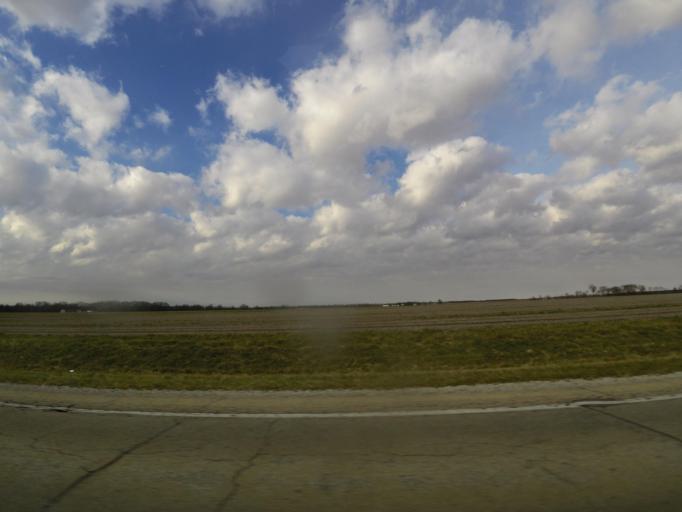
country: US
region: Illinois
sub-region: Fayette County
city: Ramsey
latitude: 39.2066
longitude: -89.1007
